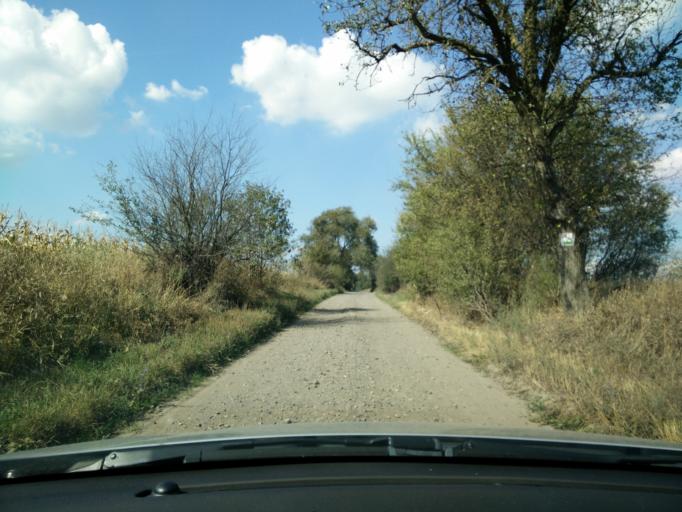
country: PL
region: Greater Poland Voivodeship
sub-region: Powiat poznanski
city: Kleszczewo
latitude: 52.2574
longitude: 17.1942
